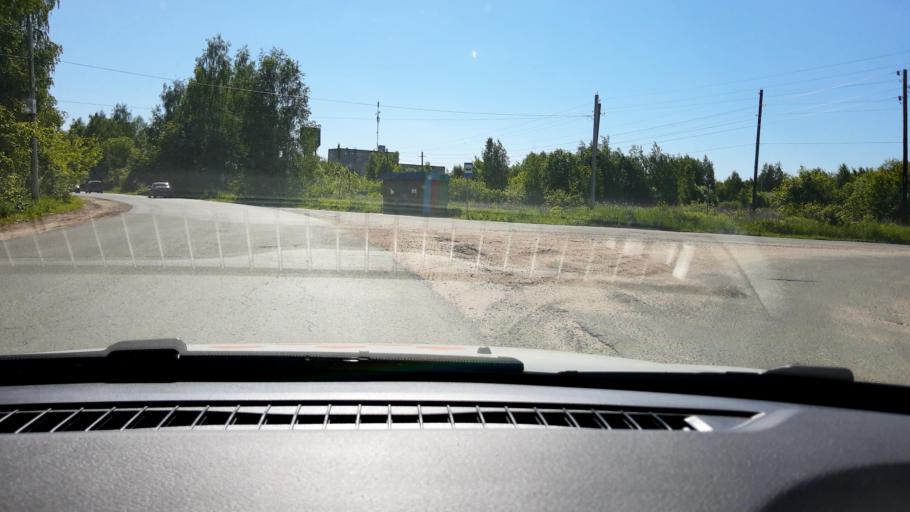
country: RU
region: Nizjnij Novgorod
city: Bor
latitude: 56.3840
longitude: 44.1440
